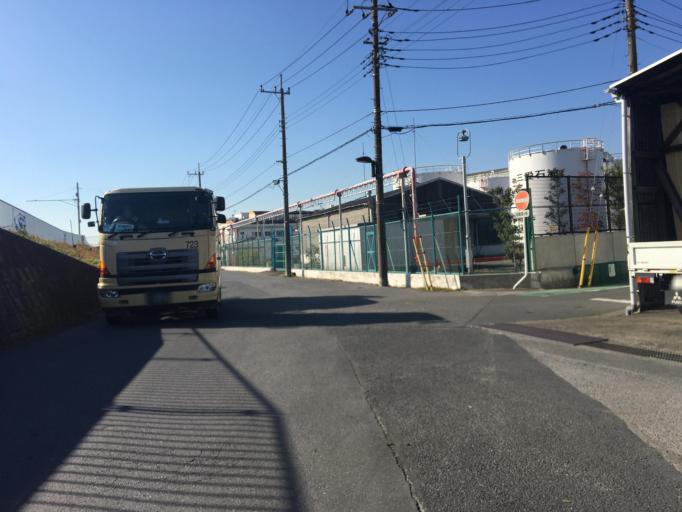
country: JP
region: Saitama
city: Yashio-shi
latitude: 35.8007
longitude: 139.8502
